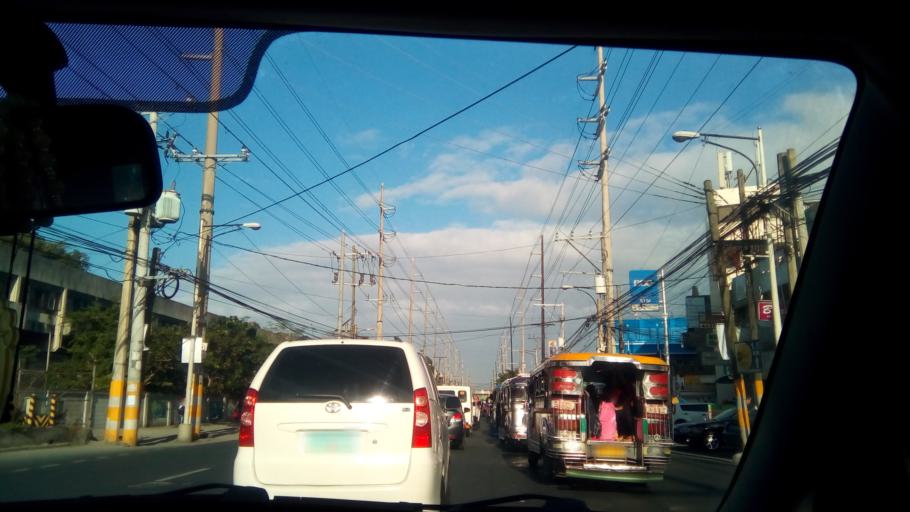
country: PH
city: Sambayanihan People's Village
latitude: 14.4353
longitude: 121.0098
